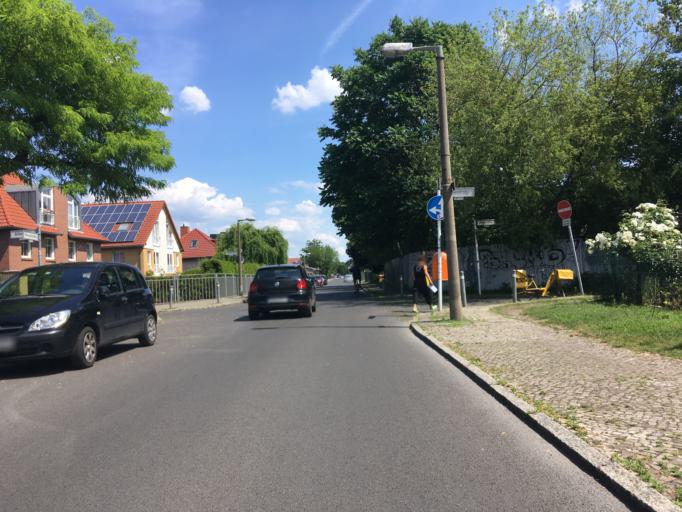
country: DE
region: Berlin
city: Karlshorst
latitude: 52.4899
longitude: 13.5356
